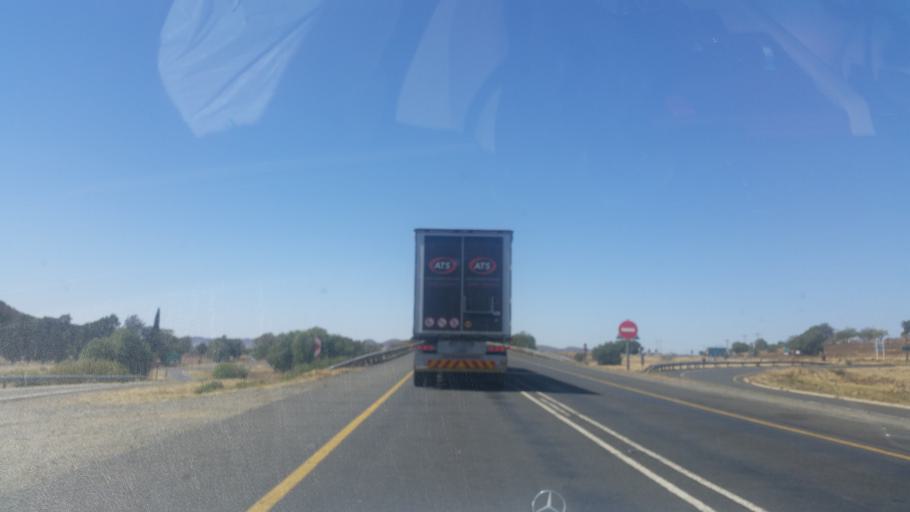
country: ZA
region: Northern Cape
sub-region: Pixley ka Seme District Municipality
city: Colesberg
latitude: -30.7106
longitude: 25.1031
